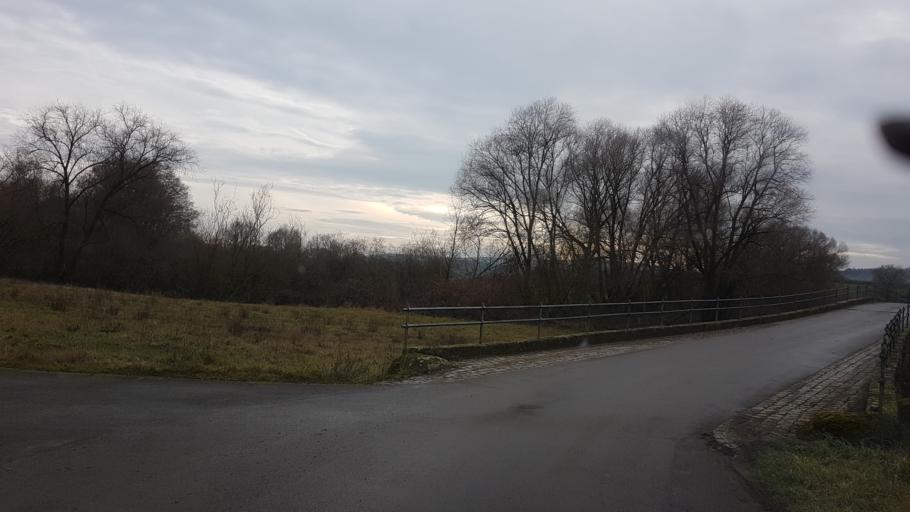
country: DE
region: Bavaria
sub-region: Upper Franconia
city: Reckendorf
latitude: 50.0057
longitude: 10.8393
